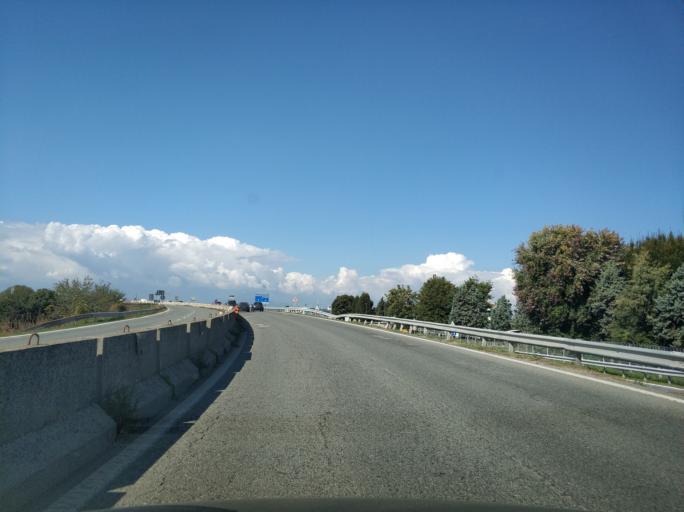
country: IT
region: Piedmont
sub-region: Provincia di Torino
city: Caselle Torinese
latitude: 45.1854
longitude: 7.6450
